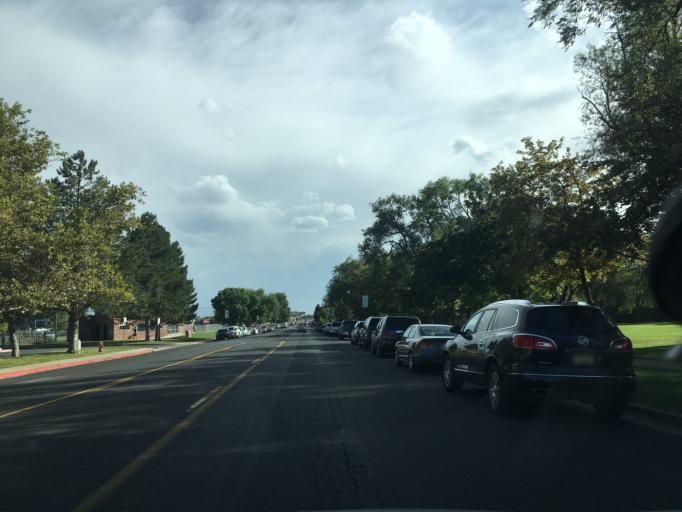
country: US
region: Utah
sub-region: Davis County
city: Layton
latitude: 41.0647
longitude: -111.9615
